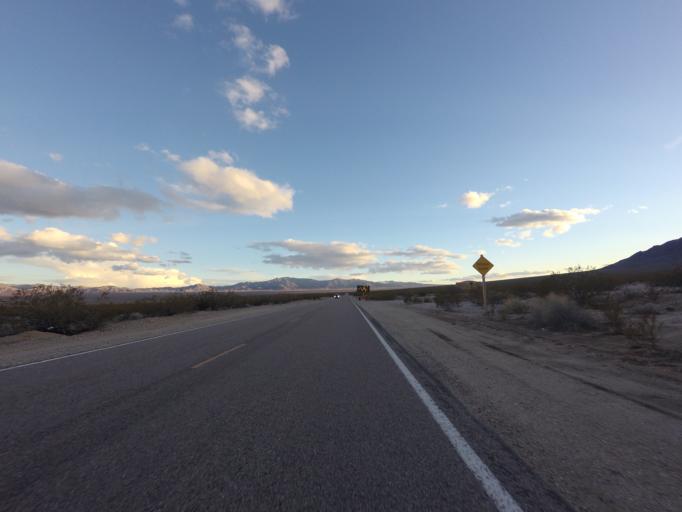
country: US
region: Nevada
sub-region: Clark County
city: Sandy Valley
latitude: 35.4499
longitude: -115.3886
